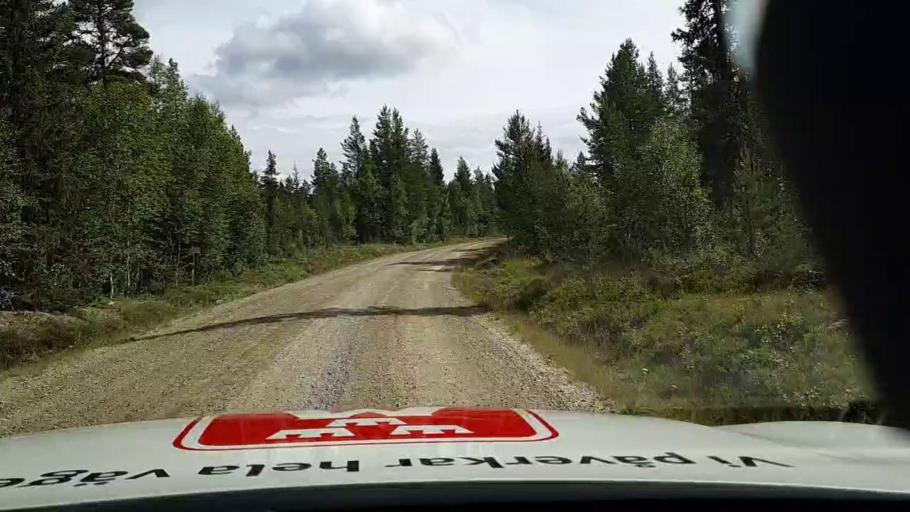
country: SE
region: Jaemtland
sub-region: Are Kommun
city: Jarpen
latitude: 62.5445
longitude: 13.4731
